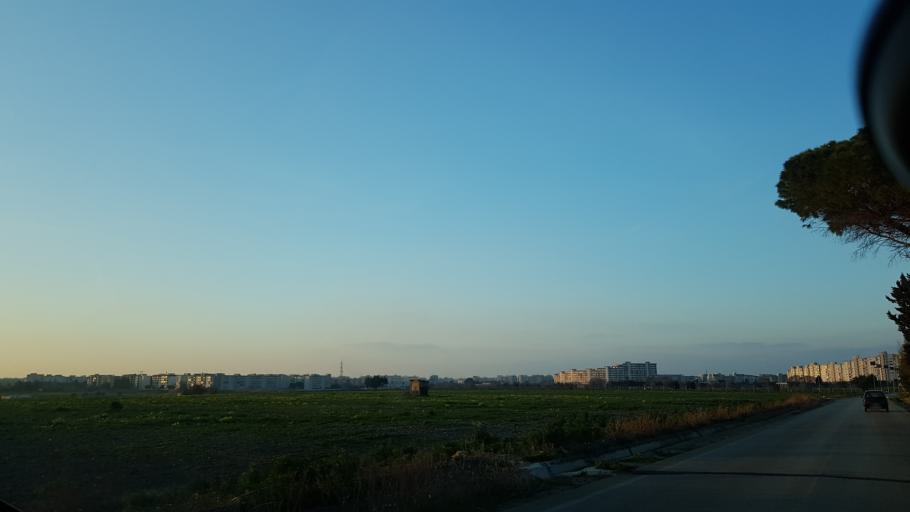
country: IT
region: Apulia
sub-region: Provincia di Brindisi
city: La Rosa
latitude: 40.6112
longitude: 17.9447
